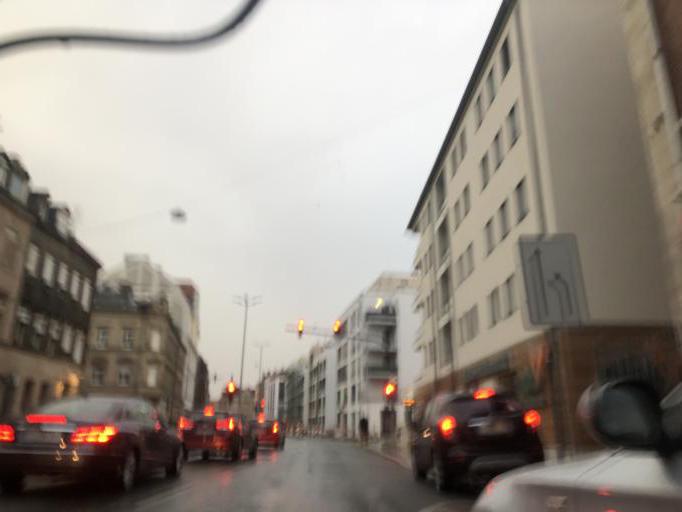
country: DE
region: Bavaria
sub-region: Regierungsbezirk Mittelfranken
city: Furth
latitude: 49.4663
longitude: 10.9858
